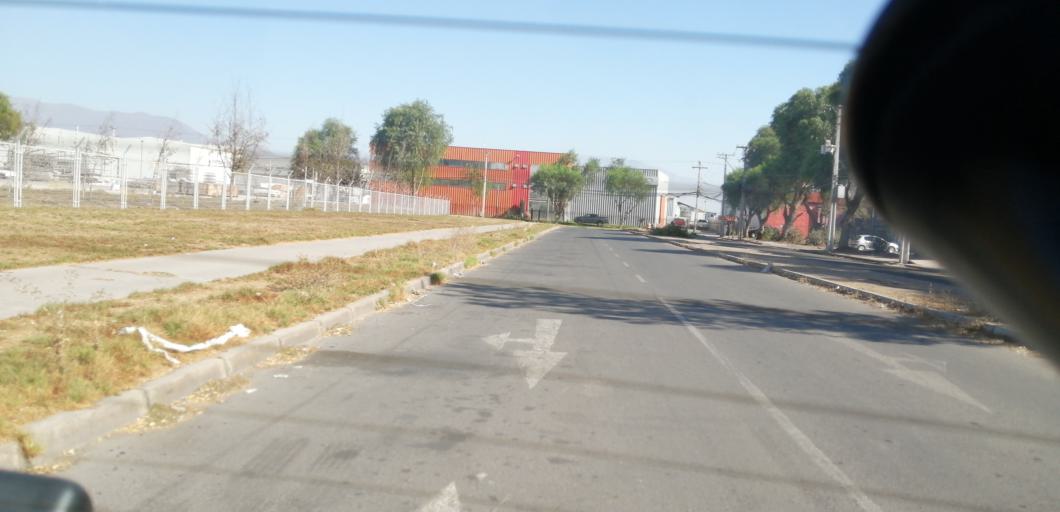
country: CL
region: Santiago Metropolitan
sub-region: Provincia de Santiago
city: Lo Prado
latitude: -33.3835
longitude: -70.7754
